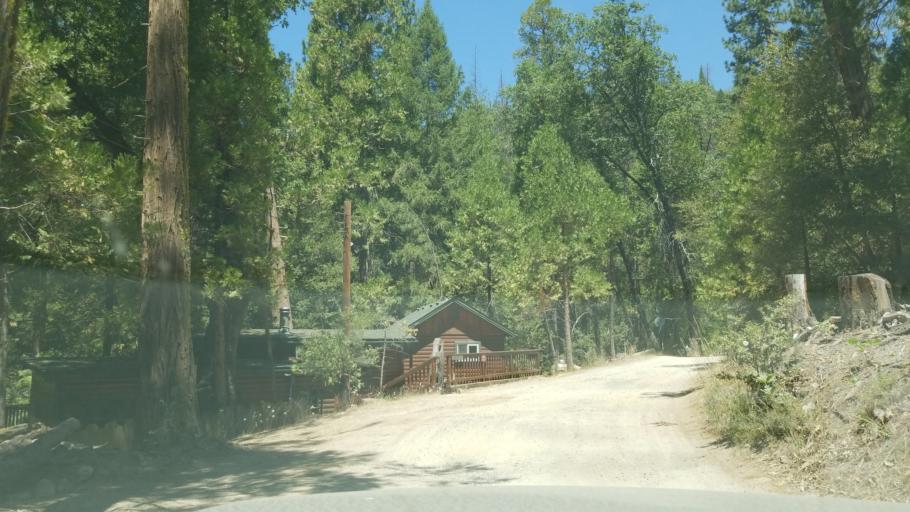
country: US
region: California
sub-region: Mariposa County
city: Yosemite Valley
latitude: 37.5478
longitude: -119.6320
